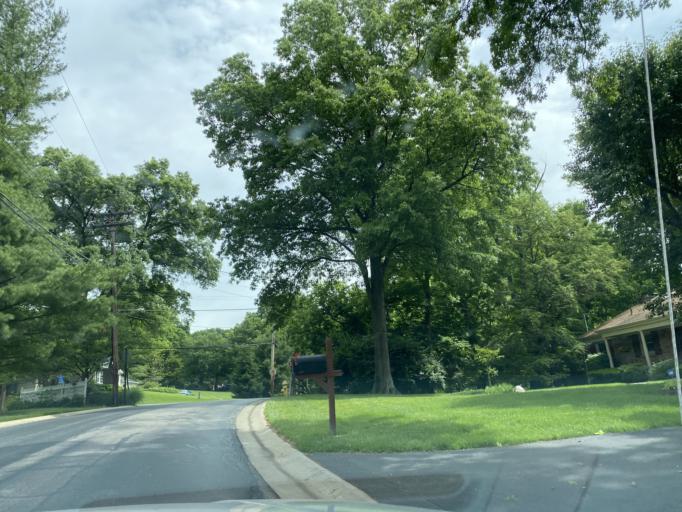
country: US
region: Ohio
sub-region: Hamilton County
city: Salem Heights
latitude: 39.0862
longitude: -84.4029
